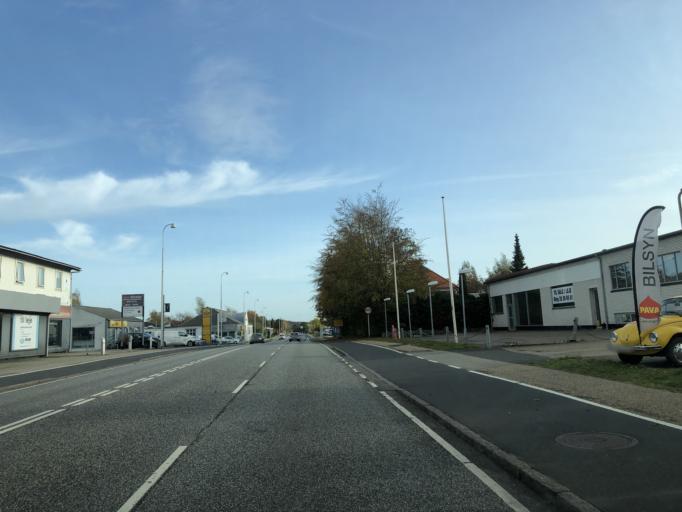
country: DK
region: Capital Region
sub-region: Rudersdal Kommune
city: Birkerod
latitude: 55.8430
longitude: 12.4364
